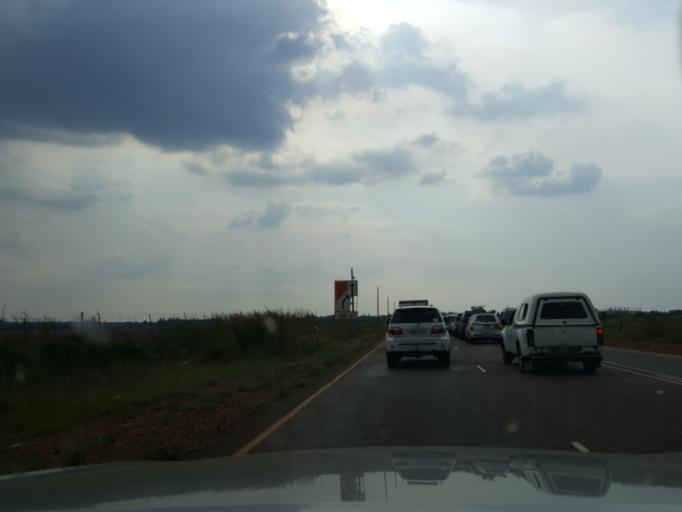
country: ZA
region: Gauteng
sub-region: City of Tshwane Metropolitan Municipality
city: Centurion
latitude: -25.8506
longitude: 28.2889
